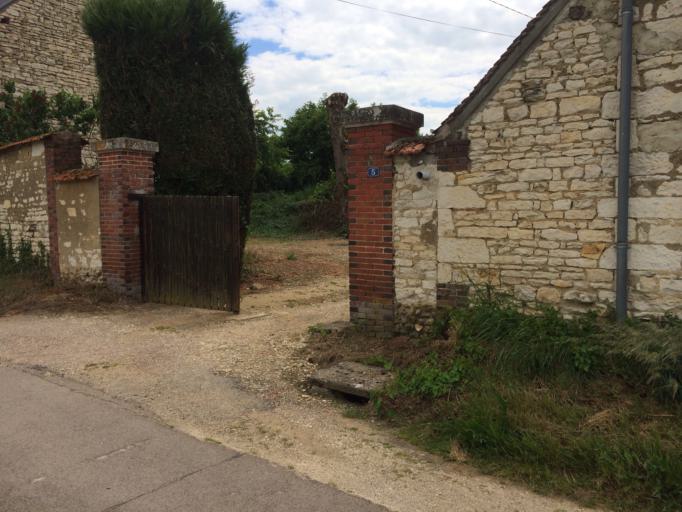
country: FR
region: Bourgogne
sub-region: Departement de l'Yonne
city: Fleury-la-Vallee
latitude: 47.8633
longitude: 3.4089
